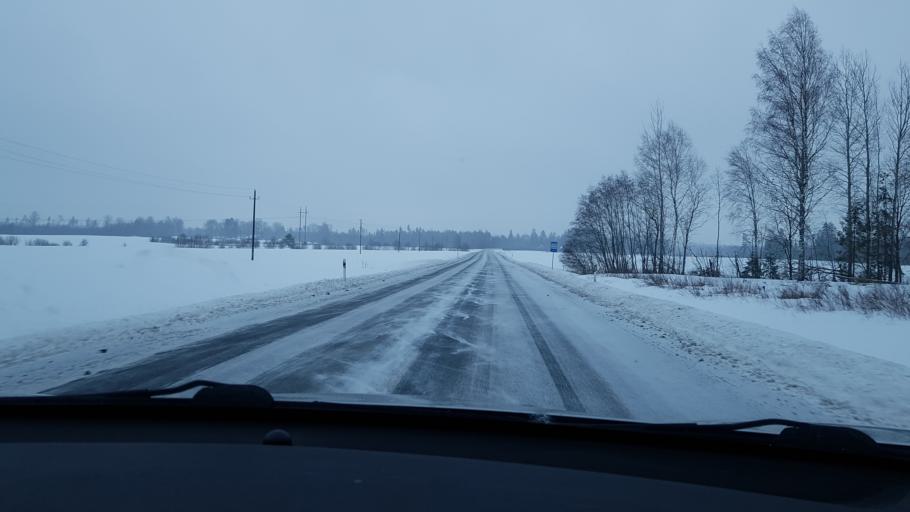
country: EE
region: Jaervamaa
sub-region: Tueri vald
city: Sarevere
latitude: 58.7244
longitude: 25.2830
